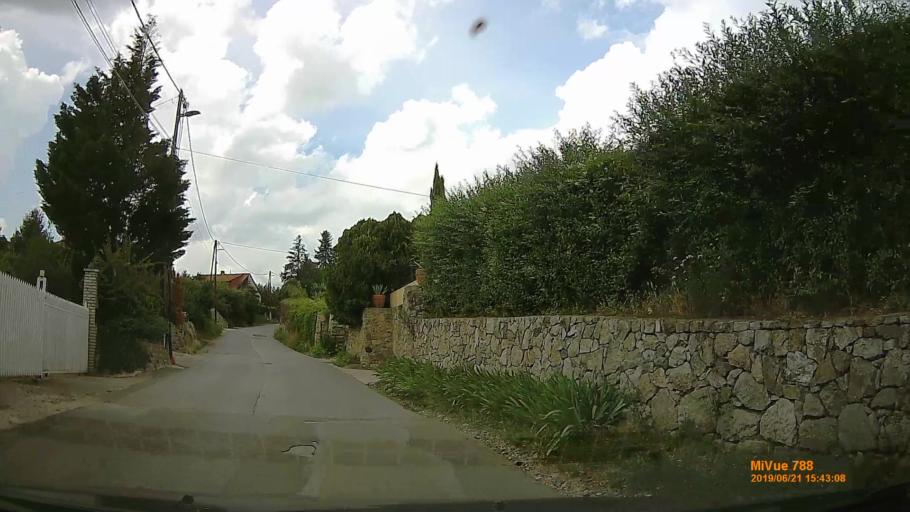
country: HU
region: Baranya
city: Pecs
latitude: 46.0838
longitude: 18.2020
